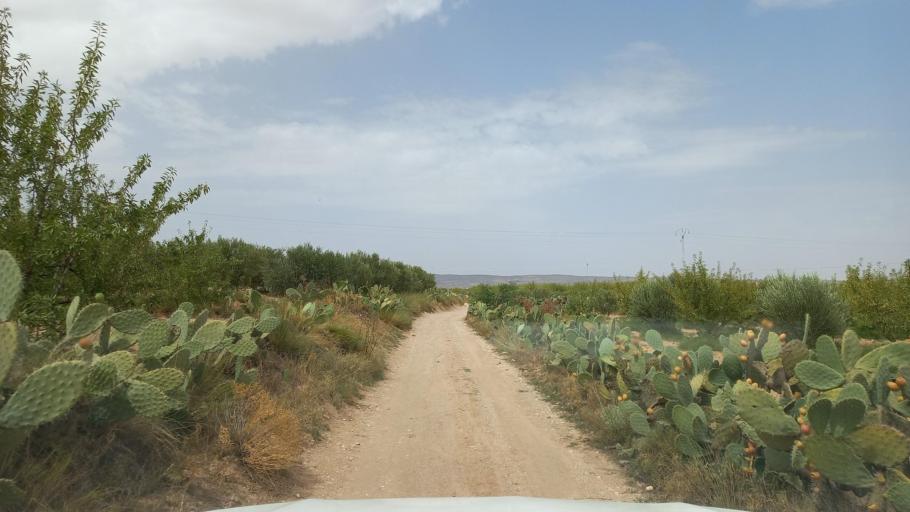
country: TN
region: Al Qasrayn
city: Kasserine
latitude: 35.2844
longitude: 9.0096
